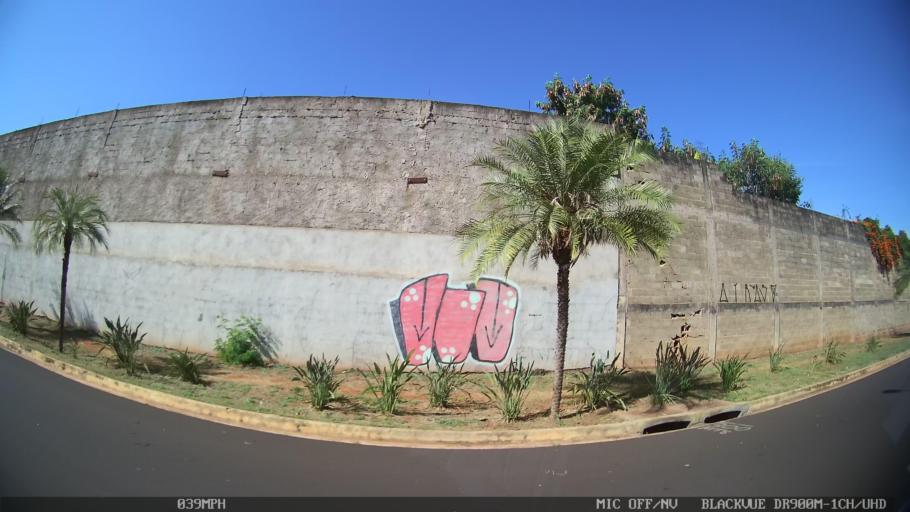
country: BR
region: Sao Paulo
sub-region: Ribeirao Preto
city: Ribeirao Preto
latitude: -21.2210
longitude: -47.7622
